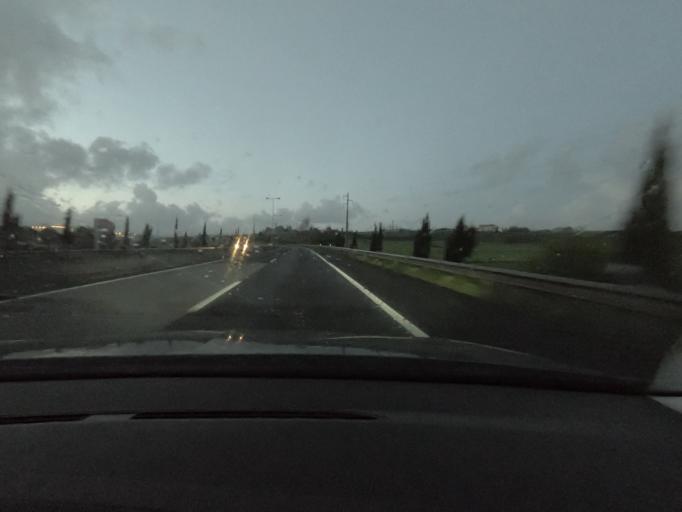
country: PT
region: Lisbon
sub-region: Oeiras
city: Porto Salvo
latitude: 38.7277
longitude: -9.2960
